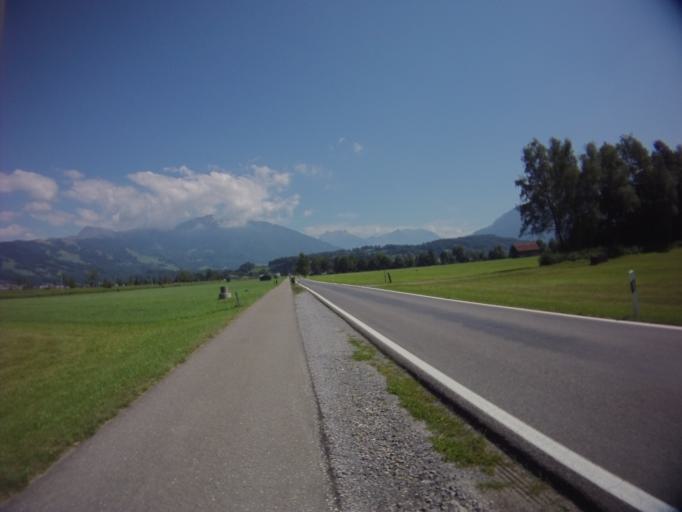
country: CH
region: Saint Gallen
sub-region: Wahlkreis See-Gaster
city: Uznach
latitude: 47.2144
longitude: 8.9943
